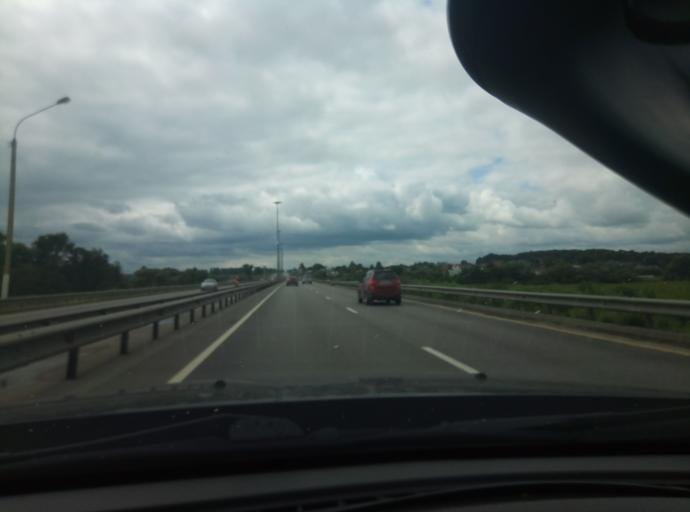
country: RU
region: Kaluga
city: Obninsk
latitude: 55.0515
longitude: 36.6118
